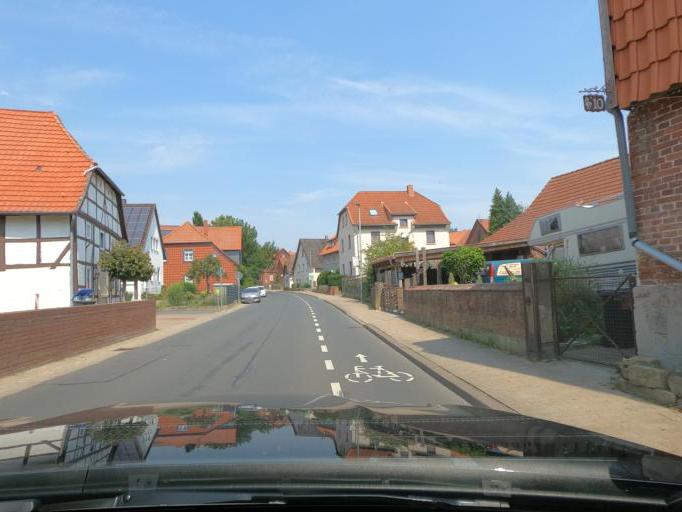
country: DE
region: Lower Saxony
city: Springe
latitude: 52.2143
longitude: 9.6279
